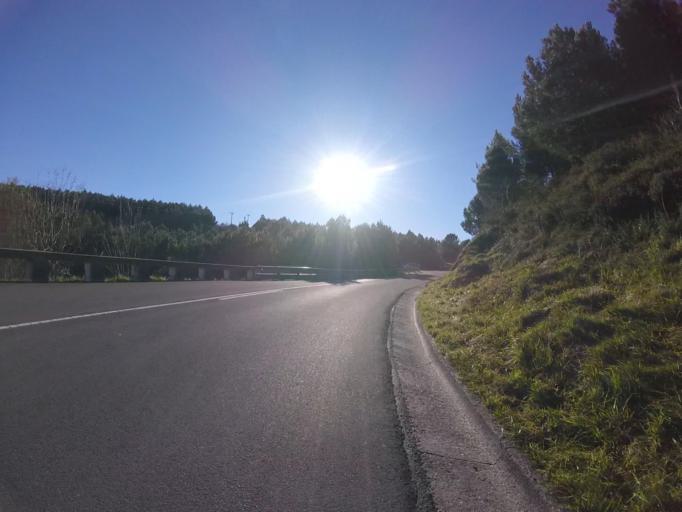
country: ES
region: Basque Country
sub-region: Provincia de Guipuzcoa
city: Lezo
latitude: 43.3358
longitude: -1.8849
